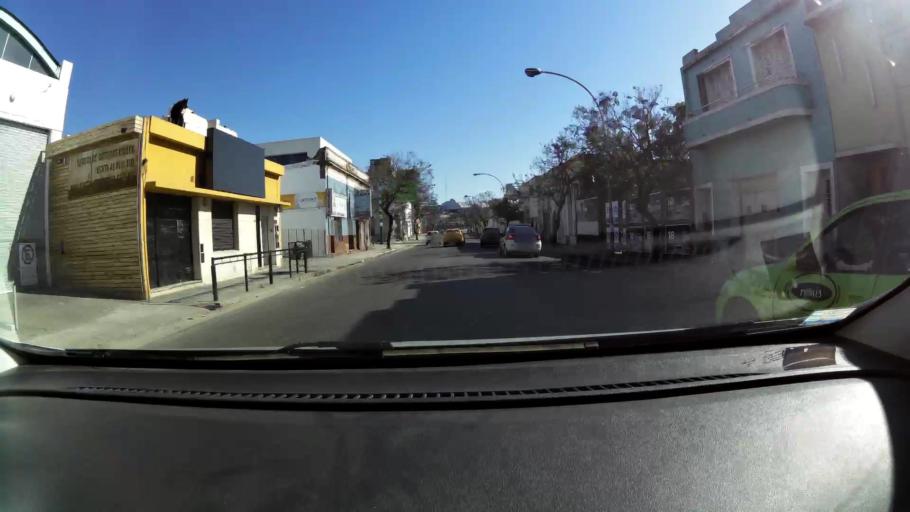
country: AR
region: Cordoba
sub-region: Departamento de Capital
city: Cordoba
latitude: -31.4096
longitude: -64.1769
